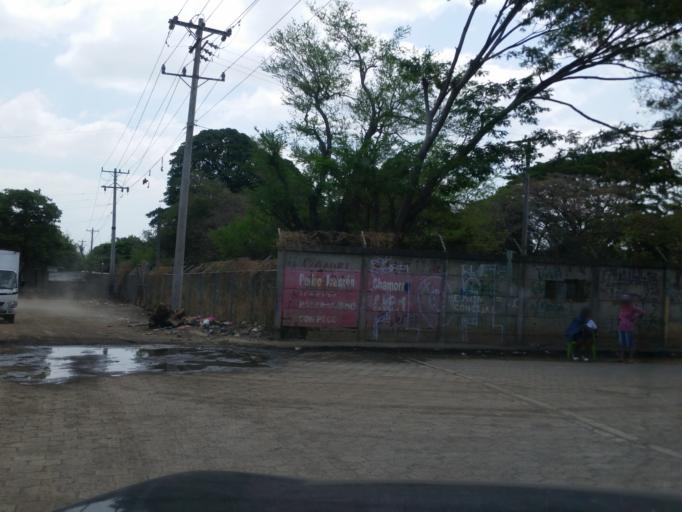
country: NI
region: Managua
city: Managua
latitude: 12.1393
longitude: -86.1913
